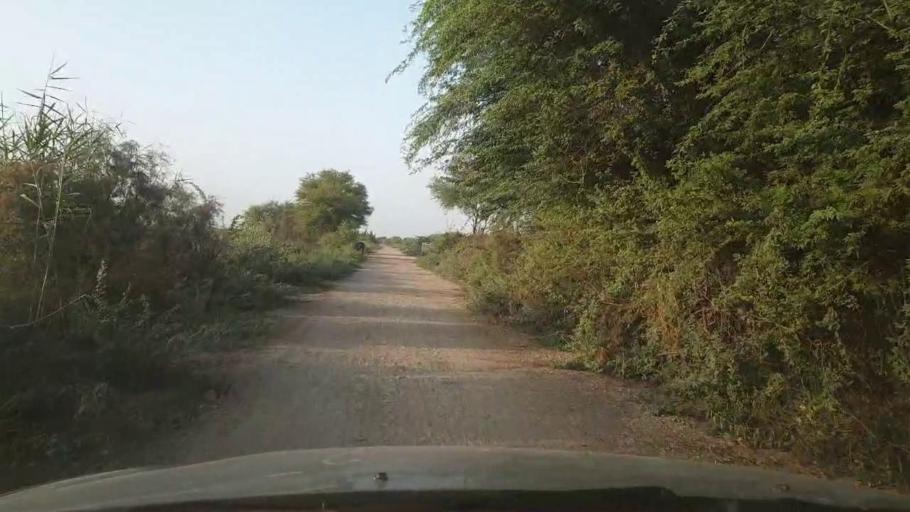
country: PK
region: Sindh
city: Tando Ghulam Ali
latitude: 25.1615
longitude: 68.9748
